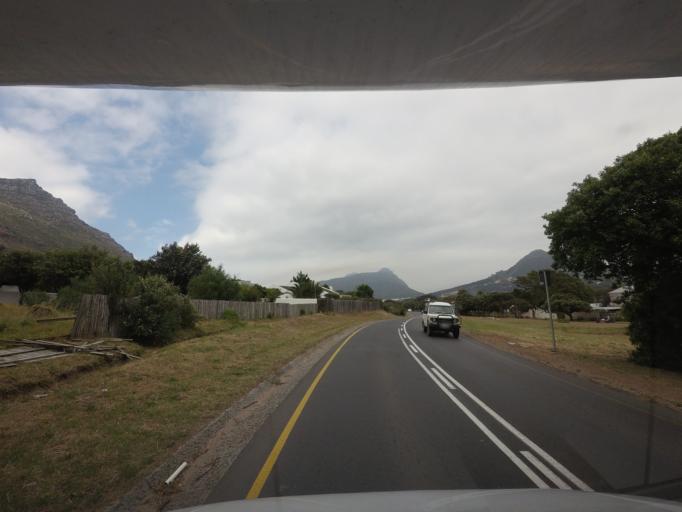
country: ZA
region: Western Cape
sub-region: City of Cape Town
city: Constantia
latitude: -34.0196
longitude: 18.3740
